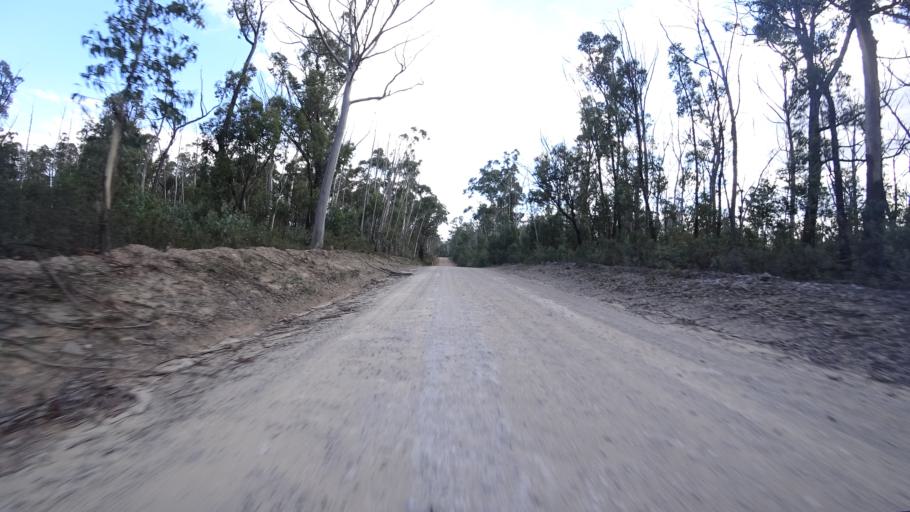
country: AU
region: New South Wales
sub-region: Lithgow
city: Lithgow
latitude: -33.4243
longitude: 150.2014
